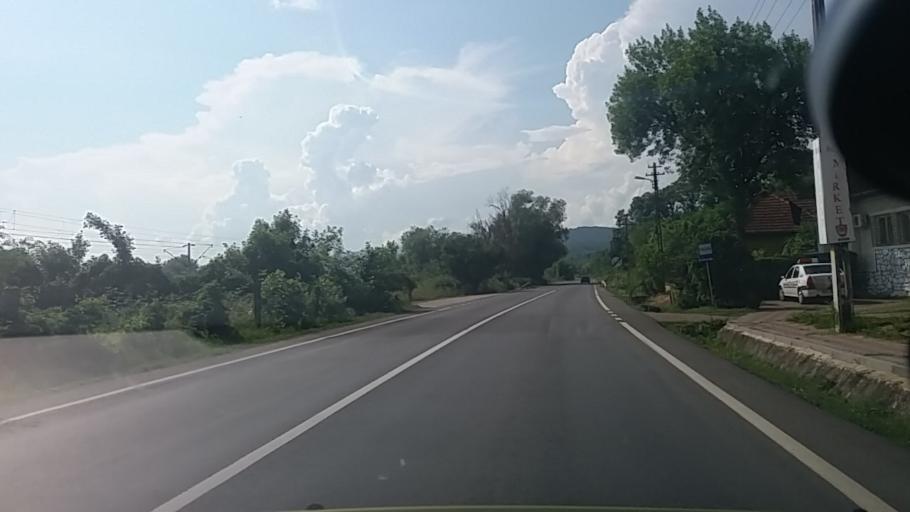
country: RO
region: Arad
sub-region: Comuna Conop
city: Conop
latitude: 46.1019
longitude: 21.8742
